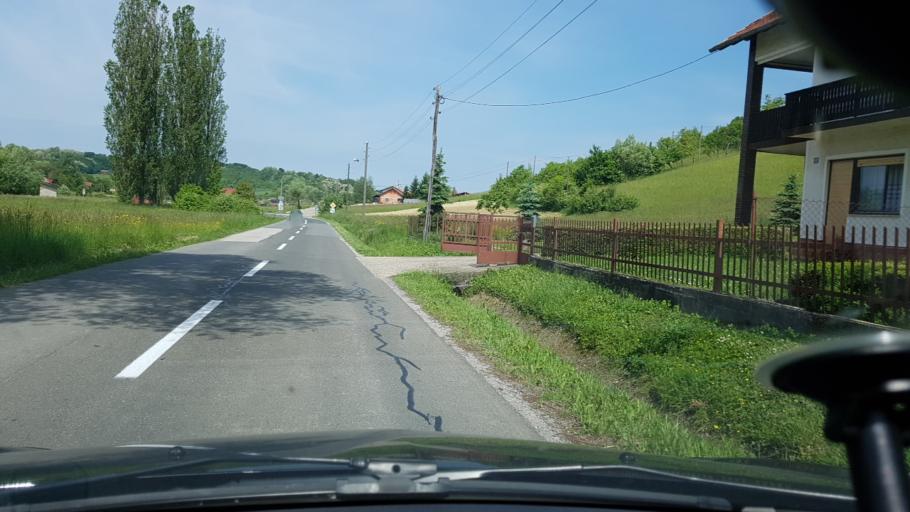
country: HR
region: Krapinsko-Zagorska
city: Marija Bistrica
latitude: 46.0066
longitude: 16.0777
